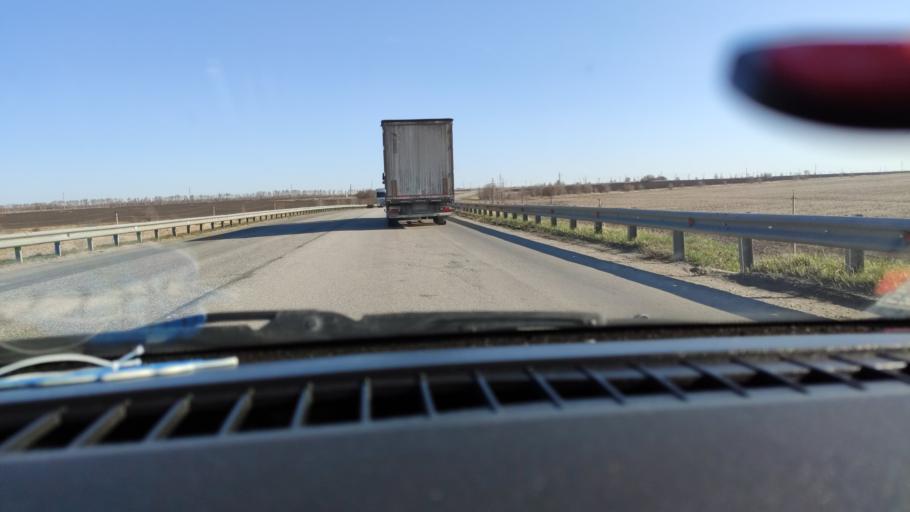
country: RU
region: Samara
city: Varlamovo
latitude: 53.1753
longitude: 48.2825
